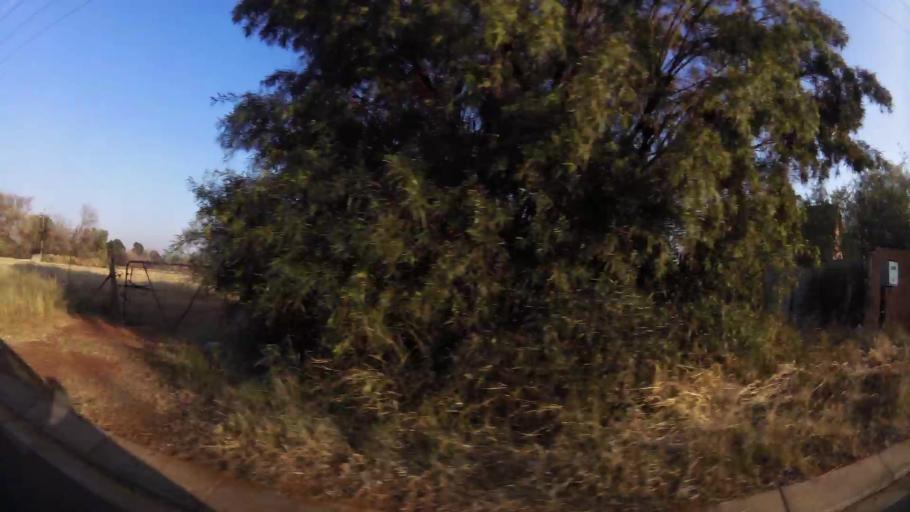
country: ZA
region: Orange Free State
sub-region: Mangaung Metropolitan Municipality
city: Bloemfontein
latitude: -29.0822
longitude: 26.1470
